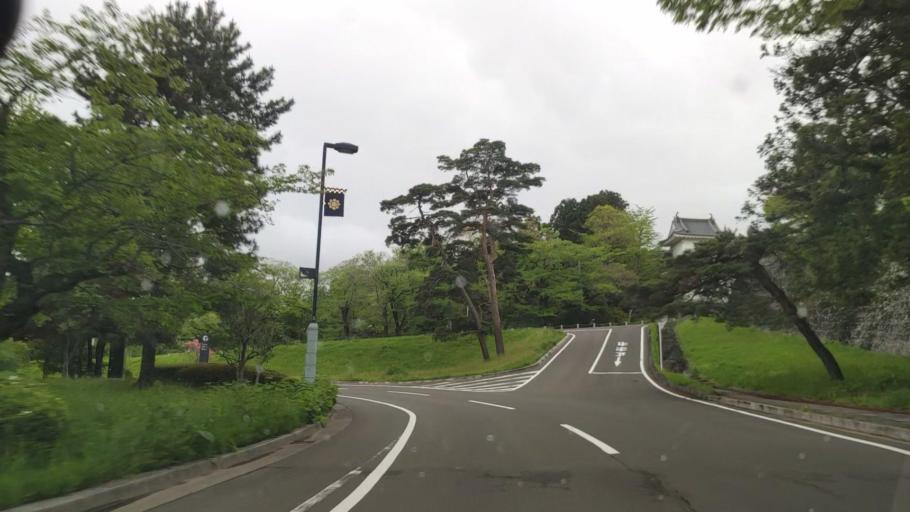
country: JP
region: Miyagi
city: Sendai
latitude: 38.2581
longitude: 140.8559
